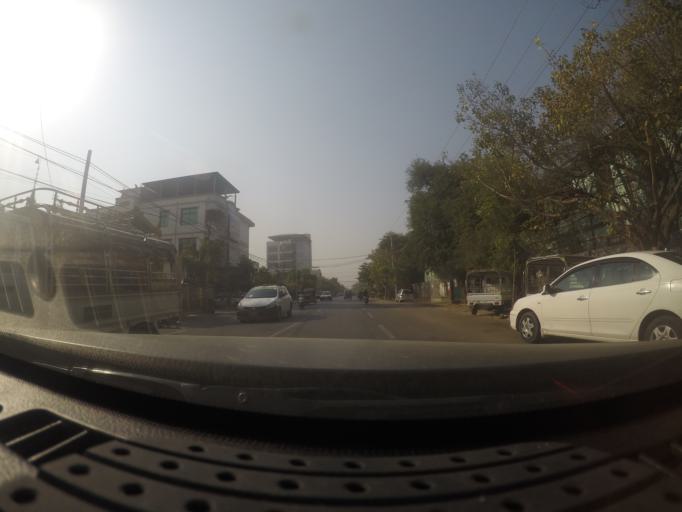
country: MM
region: Mandalay
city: Mandalay
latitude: 21.9672
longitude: 96.0802
